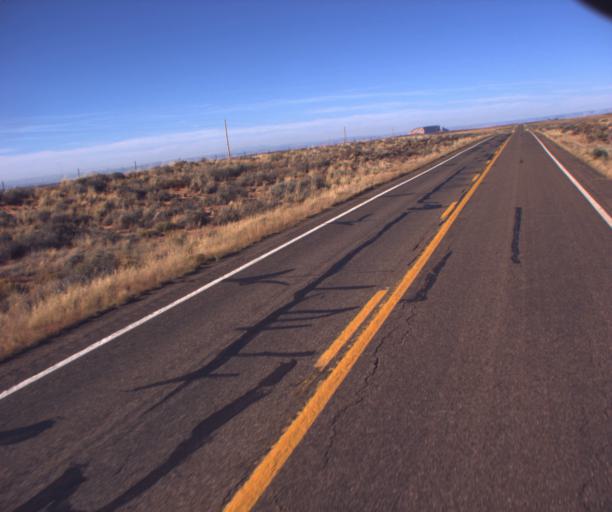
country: US
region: Arizona
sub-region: Coconino County
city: LeChee
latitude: 36.7424
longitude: -111.2846
